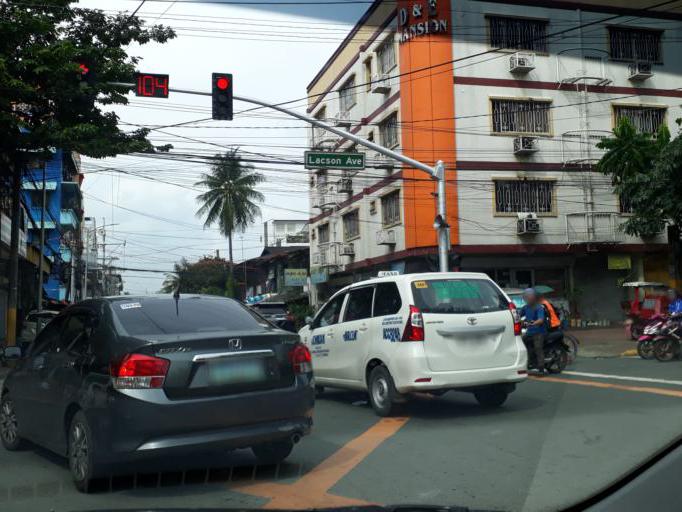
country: PH
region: Metro Manila
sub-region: City of Manila
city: Manila
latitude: 14.6084
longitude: 120.9938
